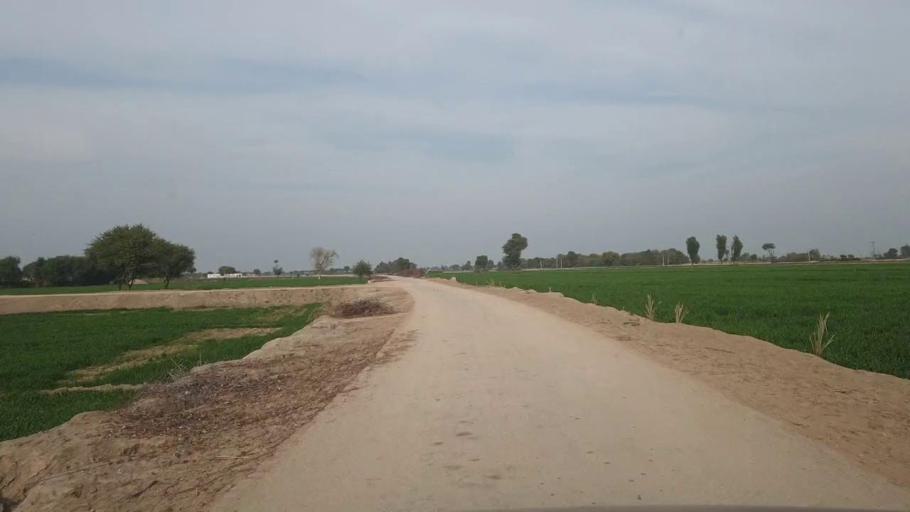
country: PK
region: Sindh
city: Shahpur Chakar
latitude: 26.1134
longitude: 68.5217
